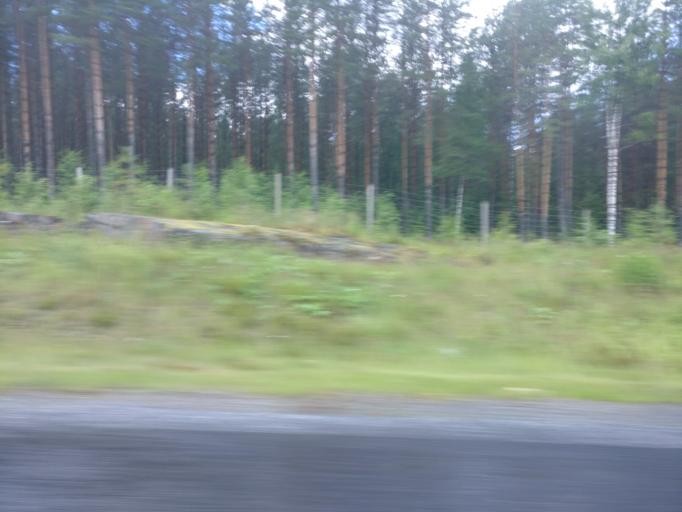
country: FI
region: Paijanne Tavastia
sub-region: Lahti
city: Hartola
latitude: 61.4688
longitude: 25.9804
